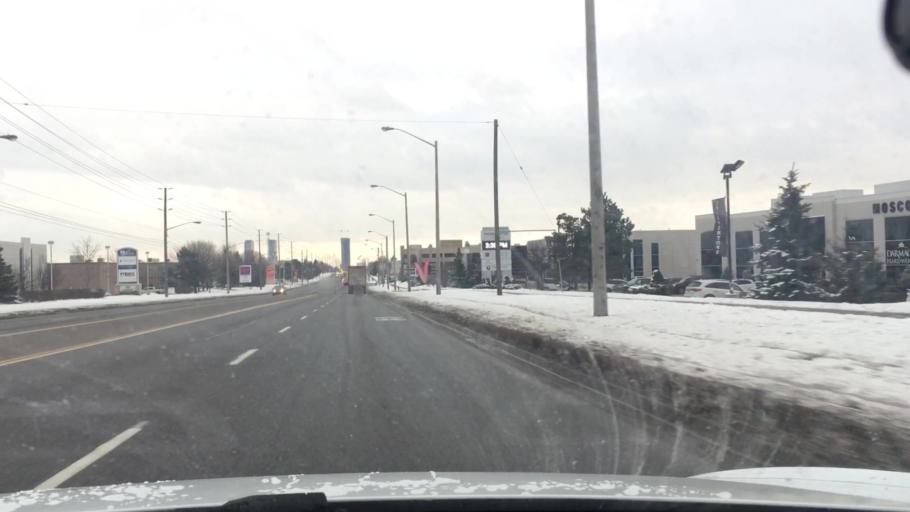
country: CA
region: Ontario
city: Vaughan
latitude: 43.8228
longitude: -79.5309
